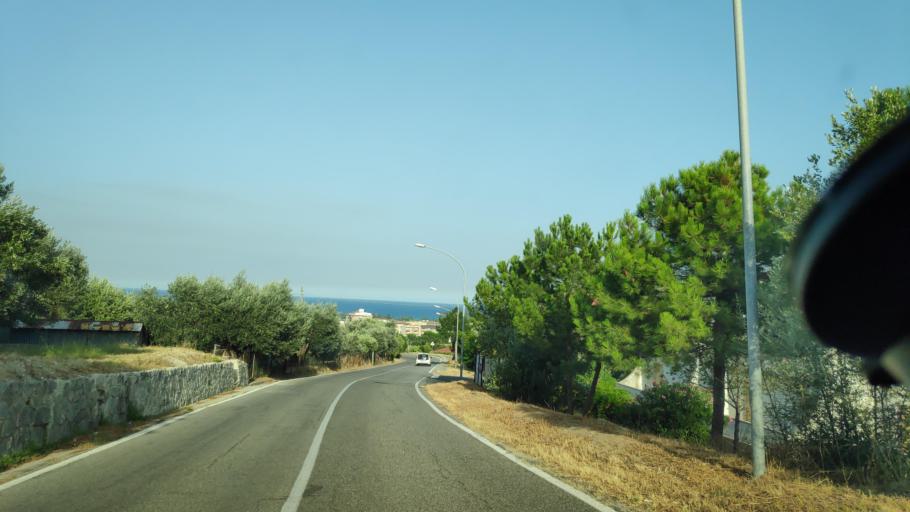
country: IT
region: Calabria
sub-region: Provincia di Catanzaro
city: Sant'Andrea Ionio Marina
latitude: 38.6197
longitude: 16.5449
